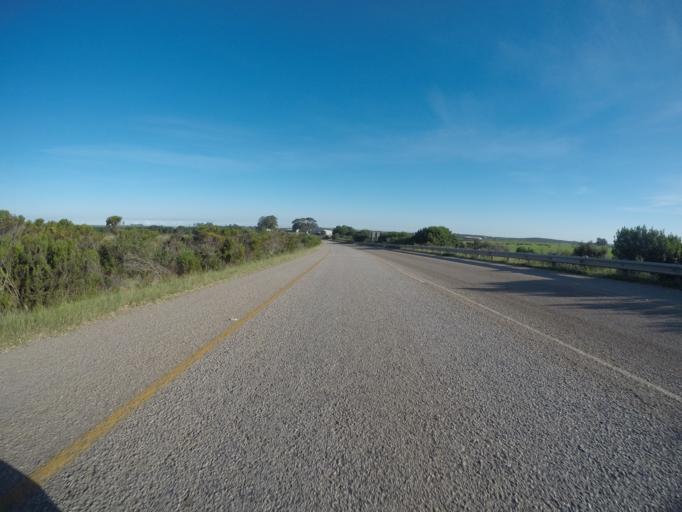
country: ZA
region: Eastern Cape
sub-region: Cacadu District Municipality
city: Kareedouw
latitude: -34.0011
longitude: 24.2347
